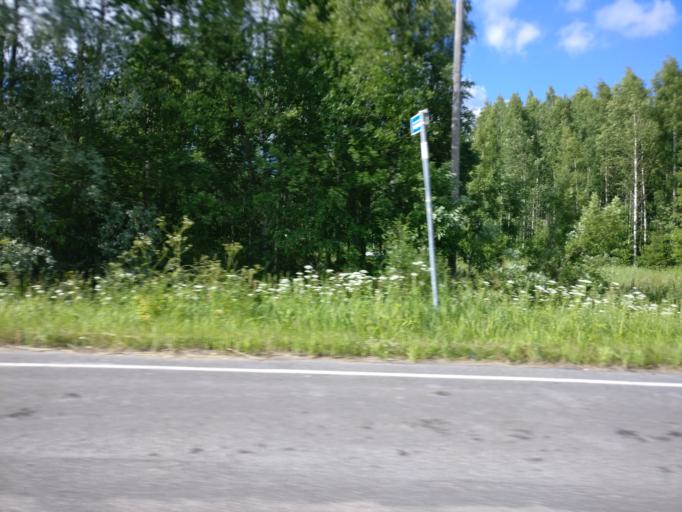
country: FI
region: Southern Savonia
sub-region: Savonlinna
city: Savonlinna
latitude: 61.8820
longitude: 29.0582
